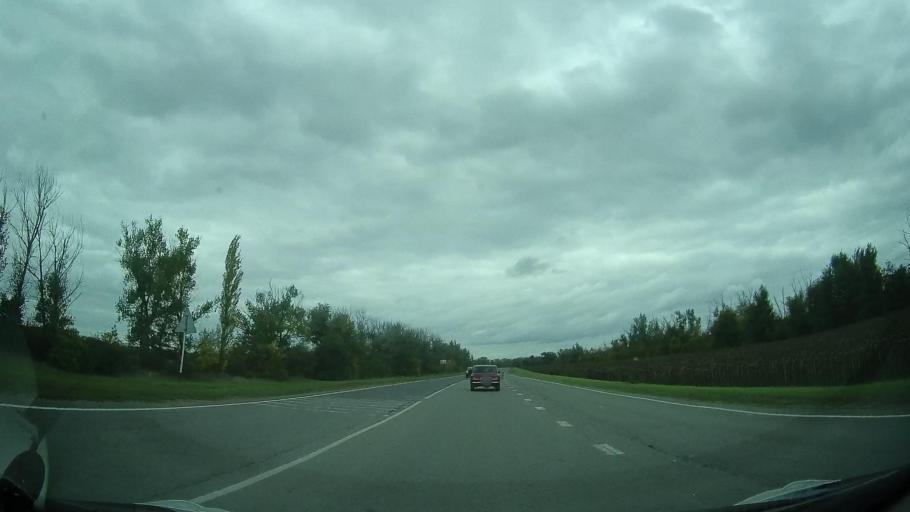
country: RU
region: Rostov
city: Yegorlykskaya
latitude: 46.5393
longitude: 40.7765
